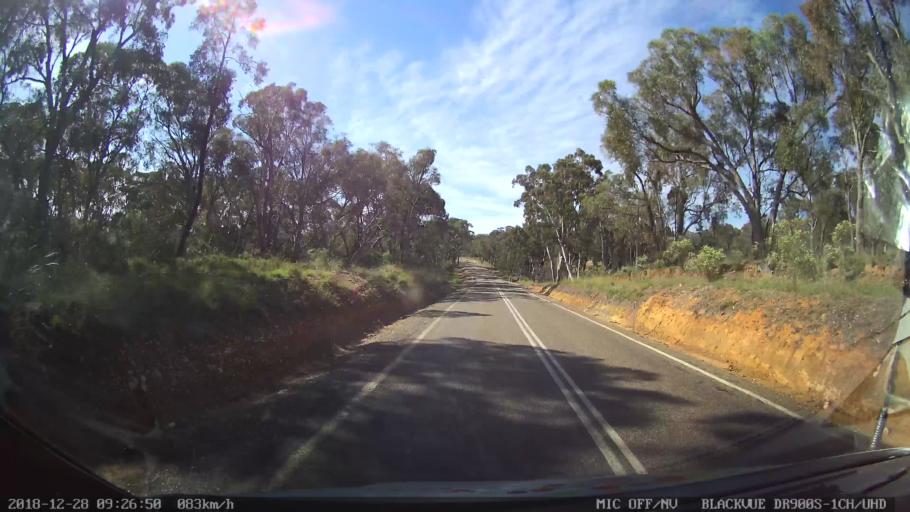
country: AU
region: New South Wales
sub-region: Upper Lachlan Shire
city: Crookwell
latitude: -34.4227
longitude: 149.4042
